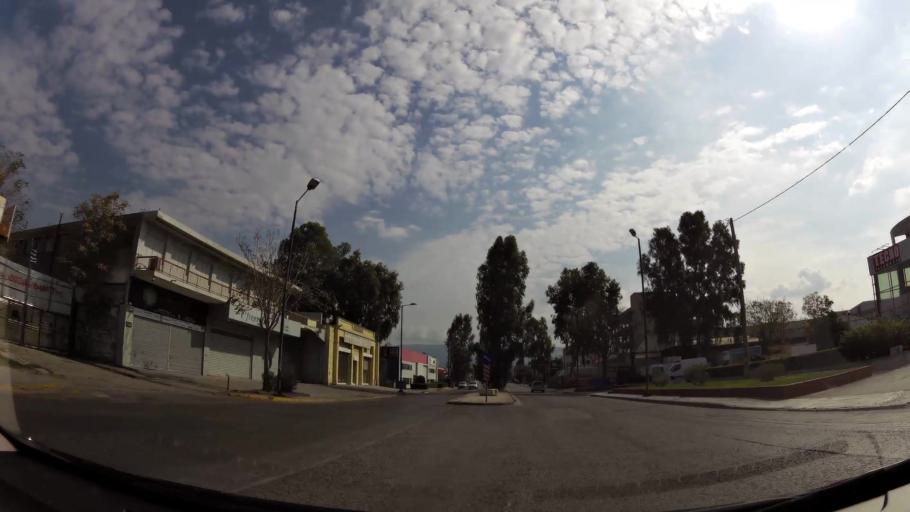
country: GR
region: Attica
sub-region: Nomarchia Athinas
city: Aigaleo
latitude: 37.9863
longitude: 23.6982
